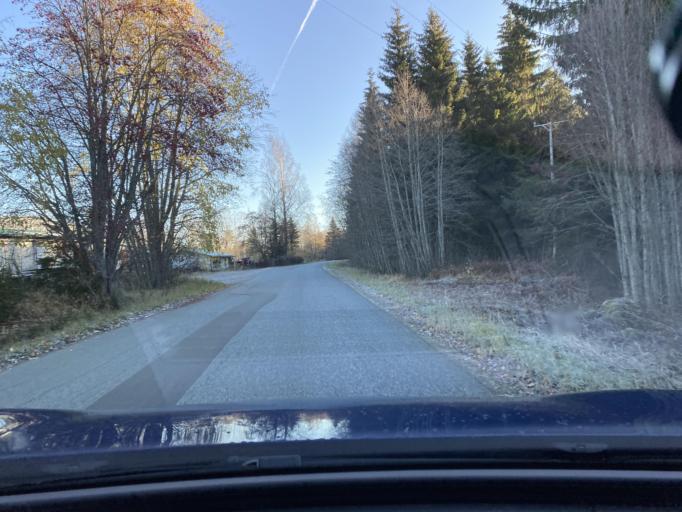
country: FI
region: Pirkanmaa
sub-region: Etelae-Pirkanmaa
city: Kylmaekoski
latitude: 61.0470
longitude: 23.7364
